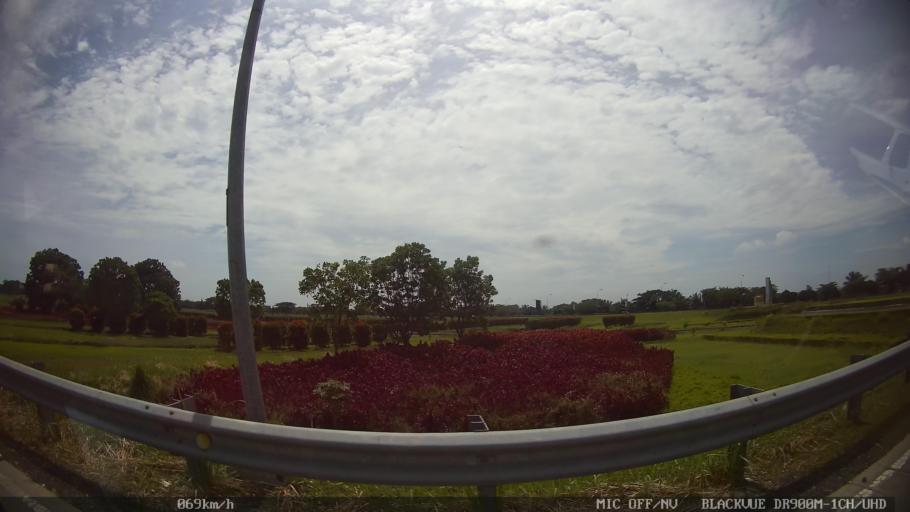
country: ID
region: North Sumatra
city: Percut
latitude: 3.6302
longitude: 98.8728
